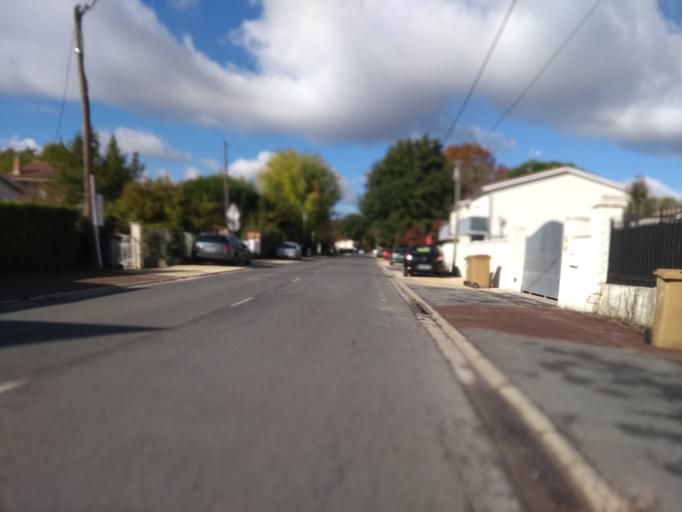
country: FR
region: Aquitaine
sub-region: Departement de la Gironde
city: Saint-Aubin-de-Medoc
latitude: 44.7731
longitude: -0.7029
